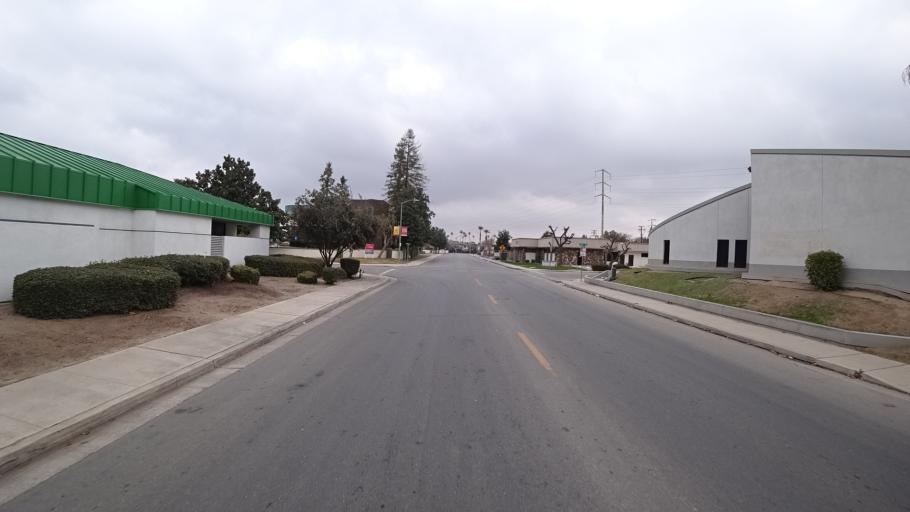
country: US
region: California
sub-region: Kern County
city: Bakersfield
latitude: 35.3959
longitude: -119.0082
